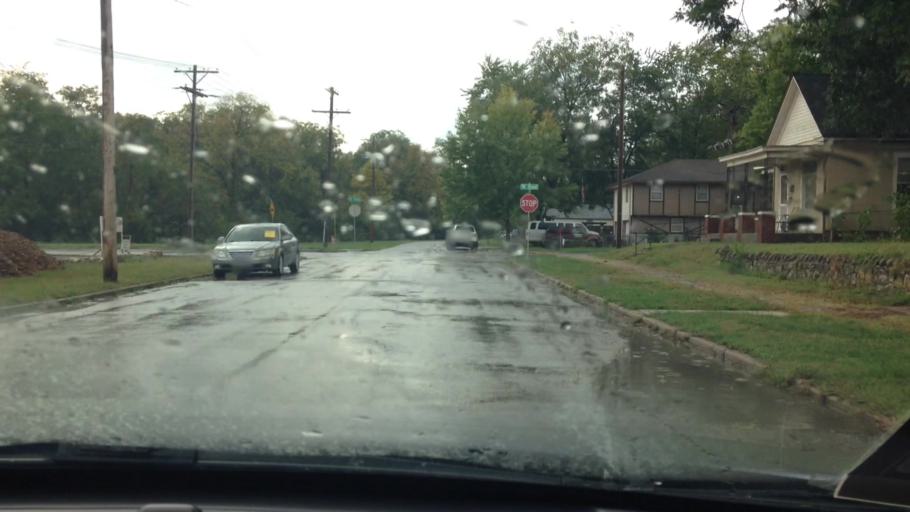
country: US
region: Kansas
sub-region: Leavenworth County
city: Leavenworth
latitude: 39.3196
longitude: -94.9277
